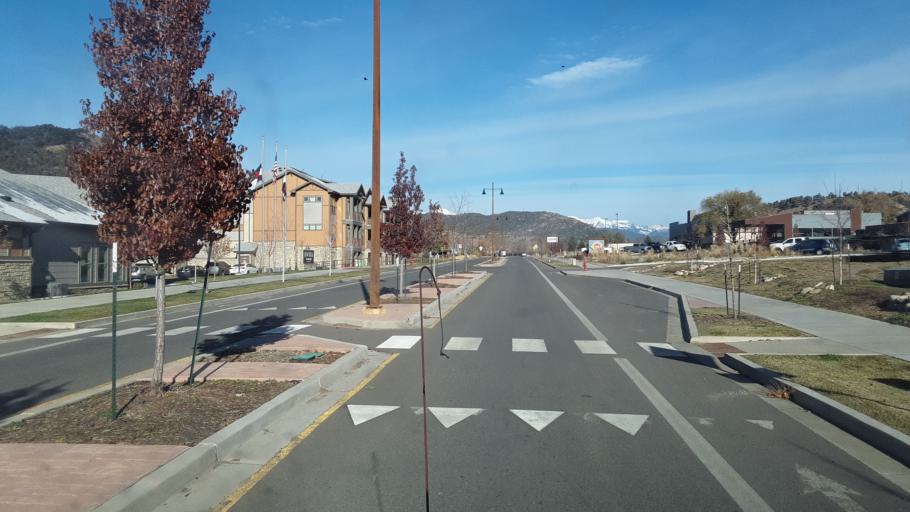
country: US
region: Colorado
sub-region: La Plata County
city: Durango
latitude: 37.2260
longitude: -107.8612
